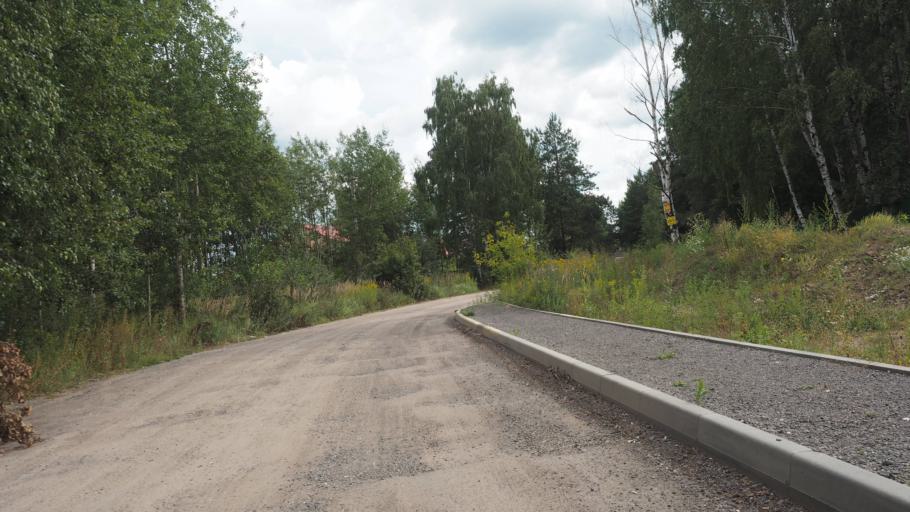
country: RU
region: Moskovskaya
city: Ramenskoye
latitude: 55.5744
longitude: 38.2697
